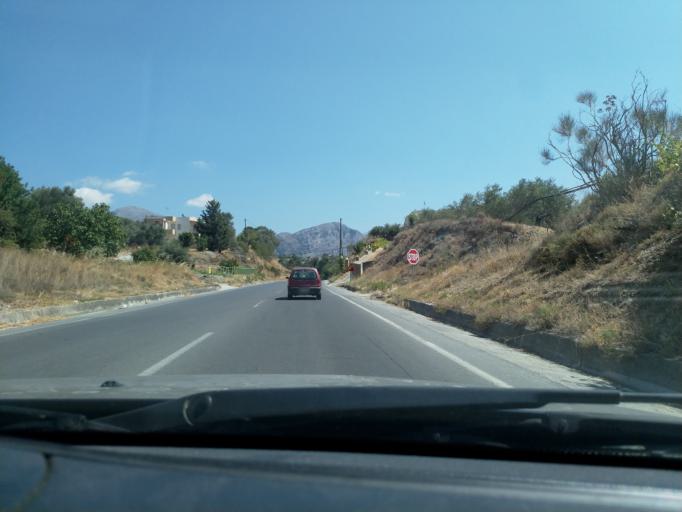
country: GR
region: Crete
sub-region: Nomos Rethymnis
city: Agia Foteini
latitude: 35.2217
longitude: 24.4950
